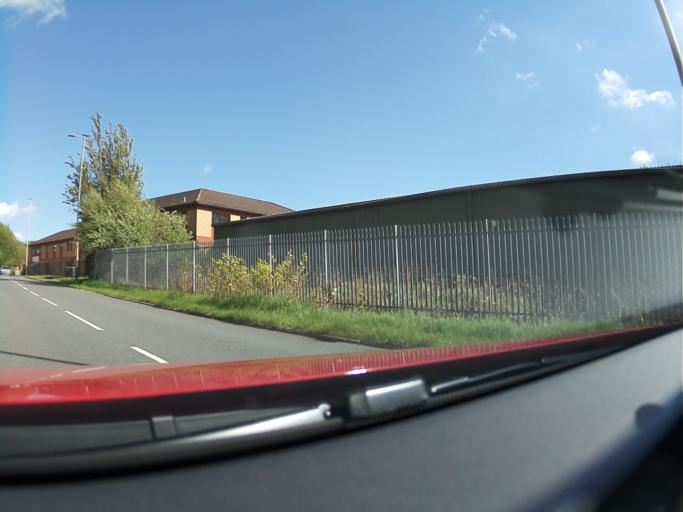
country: GB
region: Wales
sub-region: Caerphilly County Borough
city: Caerphilly
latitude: 51.5728
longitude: -3.2062
